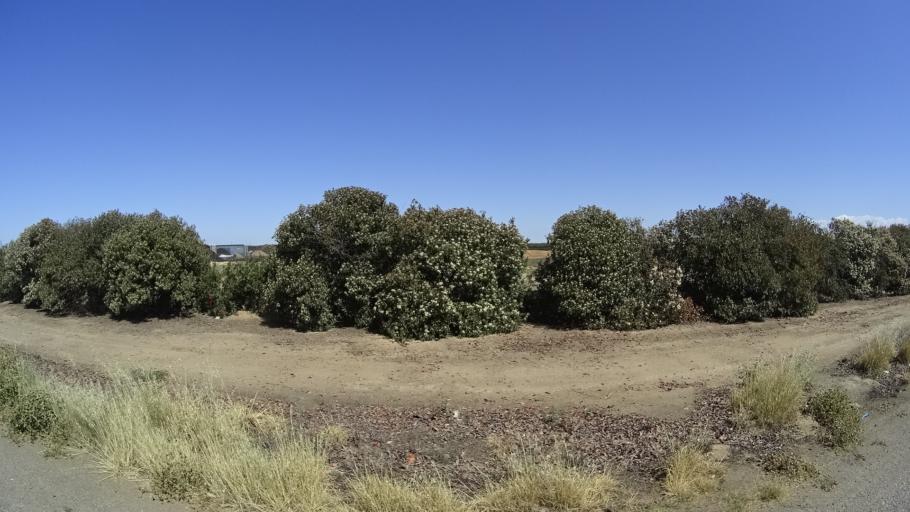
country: US
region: California
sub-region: Glenn County
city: Orland
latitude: 39.6819
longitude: -122.1568
